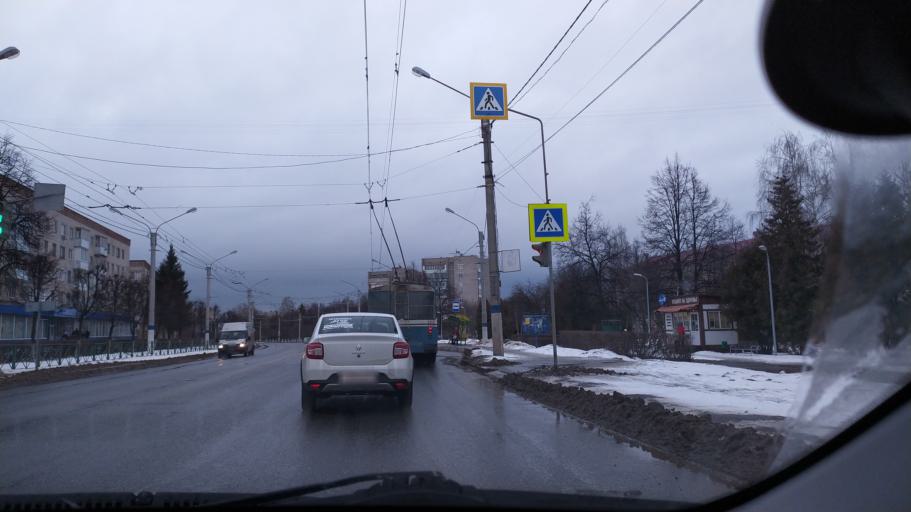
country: RU
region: Chuvashia
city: Novocheboksarsk
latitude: 56.1178
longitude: 47.4924
